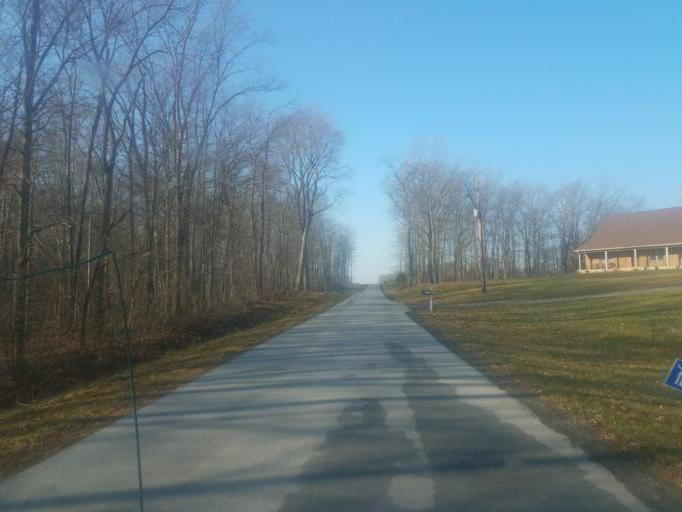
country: US
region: Ohio
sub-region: Seneca County
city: Tiffin
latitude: 41.0373
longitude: -83.0774
